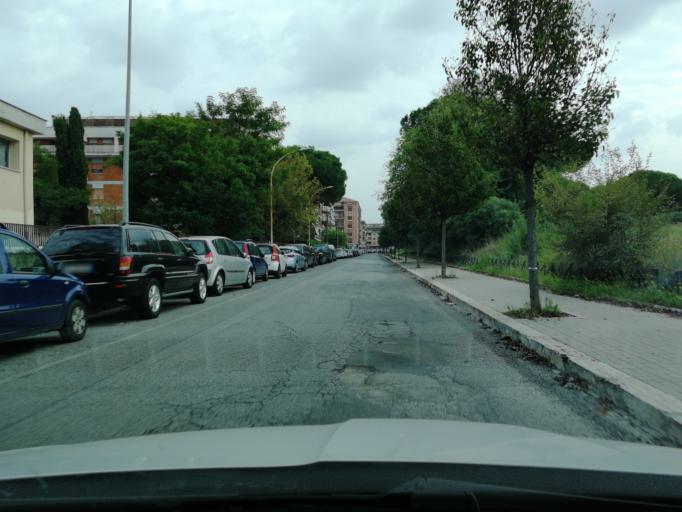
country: IT
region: Latium
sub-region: Citta metropolitana di Roma Capitale
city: Rome
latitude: 41.8548
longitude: 12.5556
